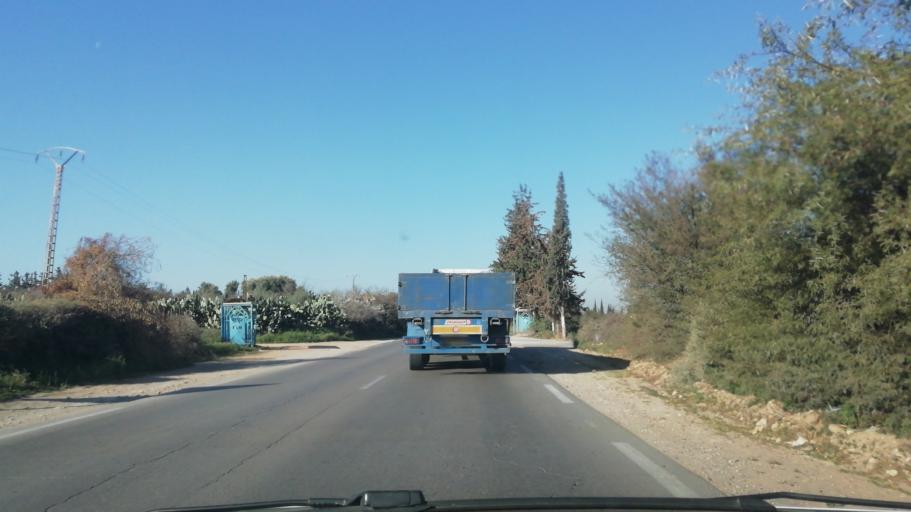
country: DZ
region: Mascara
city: Sig
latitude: 35.5755
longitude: -0.0057
